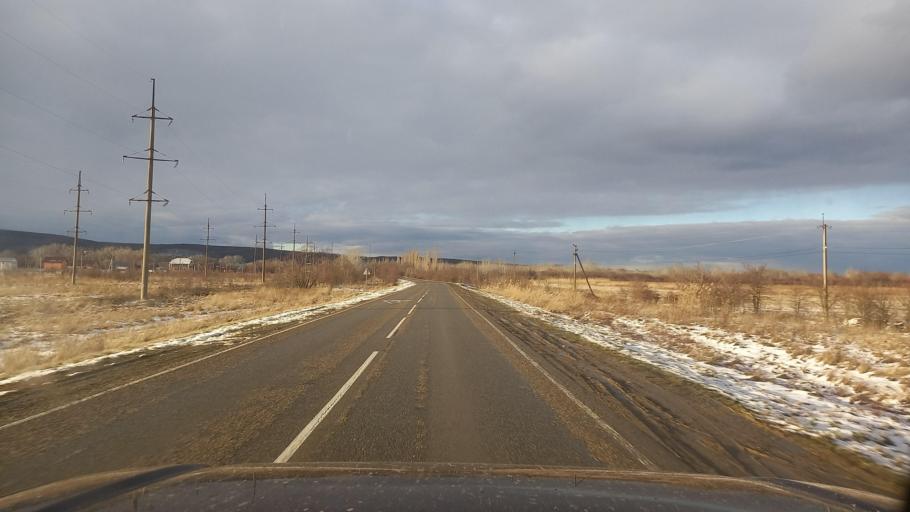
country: RU
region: Krasnodarskiy
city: Smolenskaya
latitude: 44.7739
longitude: 38.8161
